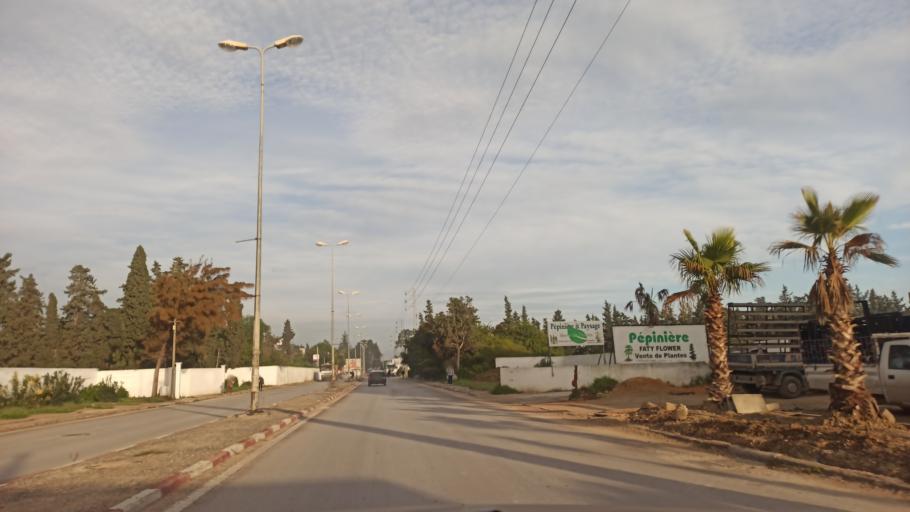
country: TN
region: Ariana
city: Ariana
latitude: 36.8729
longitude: 10.2472
